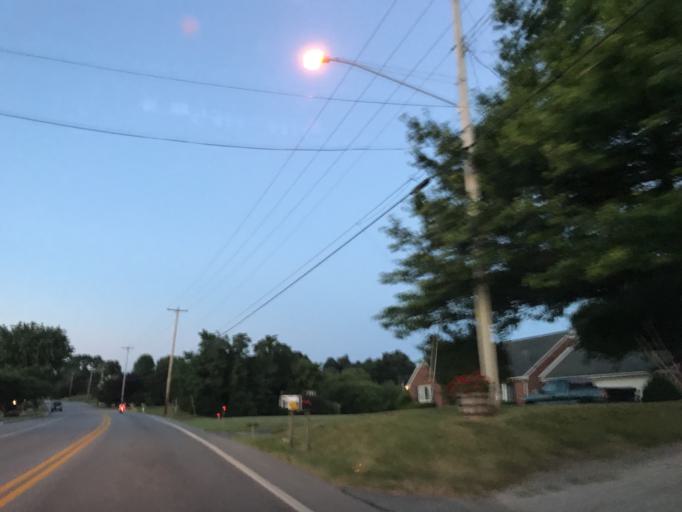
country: US
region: Pennsylvania
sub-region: York County
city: Parkville
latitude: 39.8015
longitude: -76.9456
